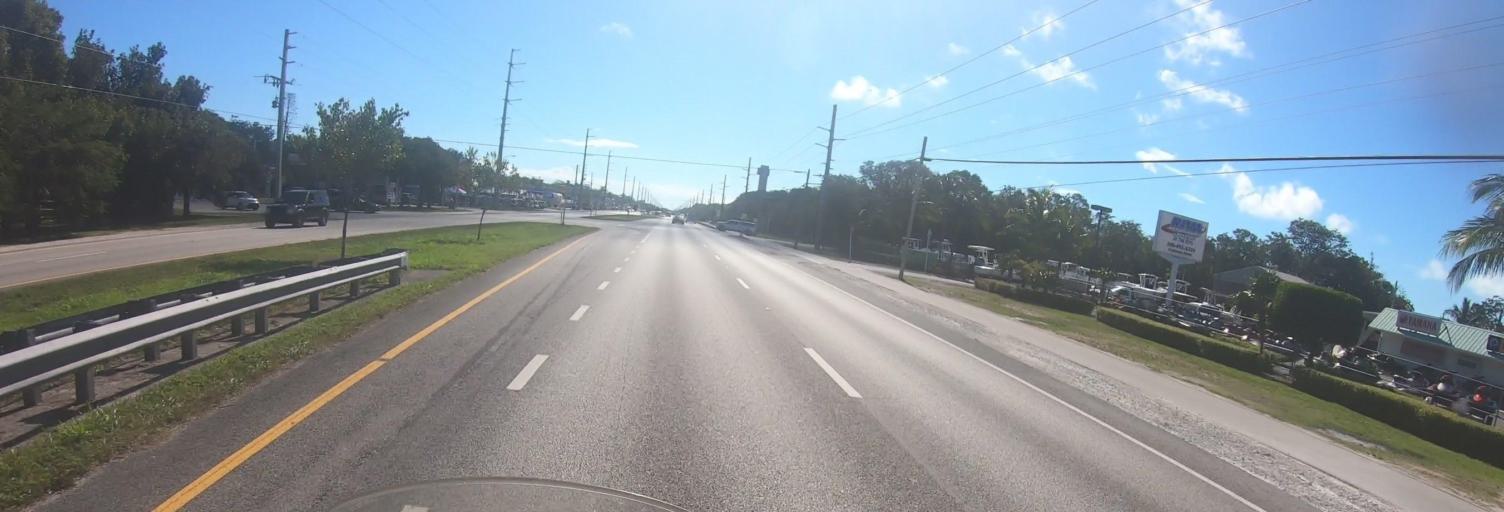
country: US
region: Florida
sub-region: Monroe County
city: Key Largo
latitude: 25.1265
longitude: -80.4114
